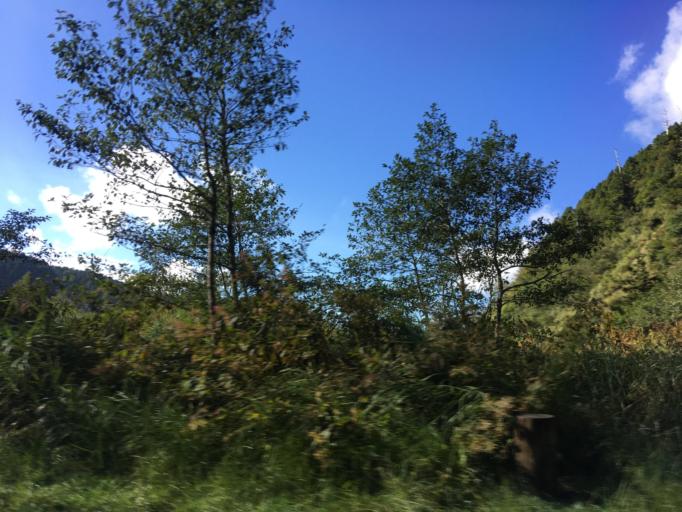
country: TW
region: Taiwan
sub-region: Yilan
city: Yilan
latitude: 24.5193
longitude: 121.5729
